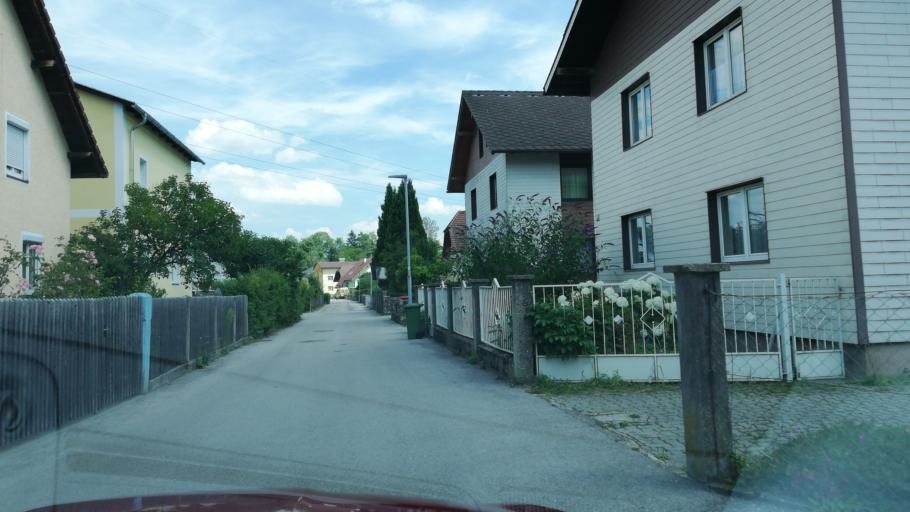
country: AT
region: Upper Austria
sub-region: Politischer Bezirk Vocklabruck
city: Vocklabruck
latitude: 47.9940
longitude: 13.6412
